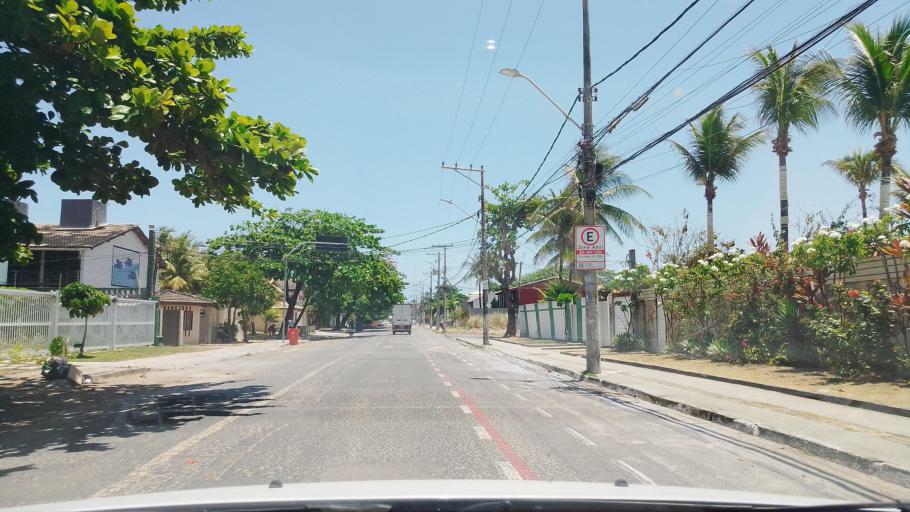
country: BR
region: Bahia
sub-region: Lauro De Freitas
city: Lauro de Freitas
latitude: -12.9319
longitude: -38.3235
